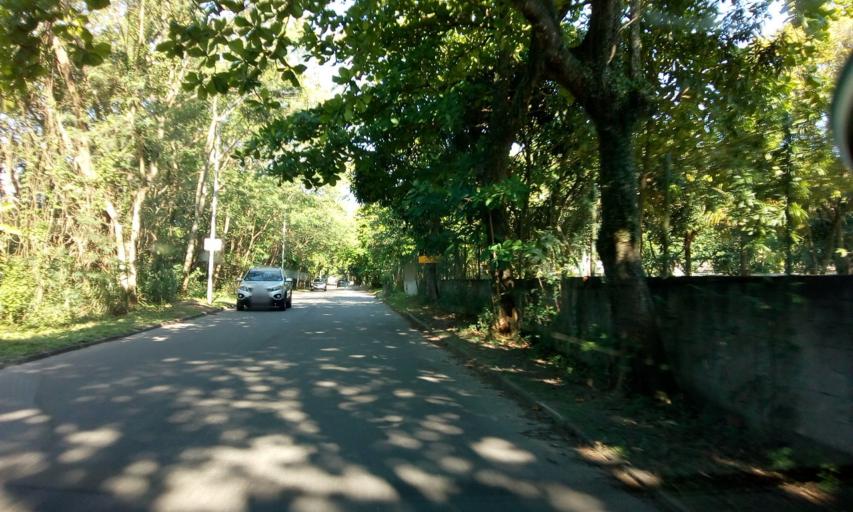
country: BR
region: Rio de Janeiro
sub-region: Nilopolis
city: Nilopolis
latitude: -22.9950
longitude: -43.3882
